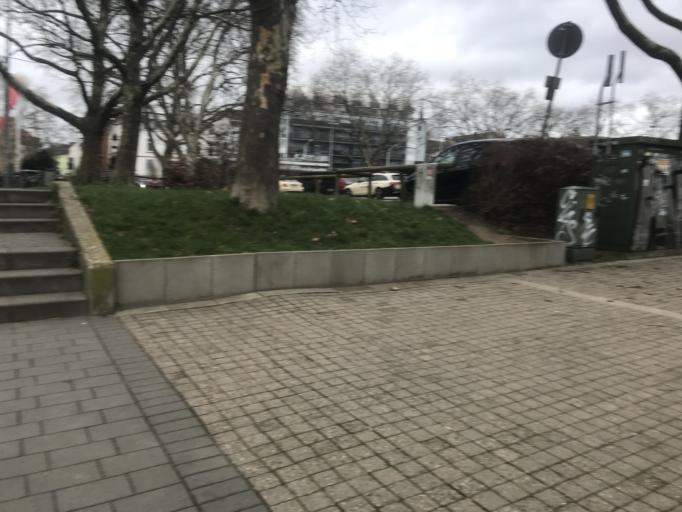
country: DE
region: Hesse
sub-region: Regierungsbezirk Darmstadt
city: Darmstadt
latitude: 49.8723
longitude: 8.6609
